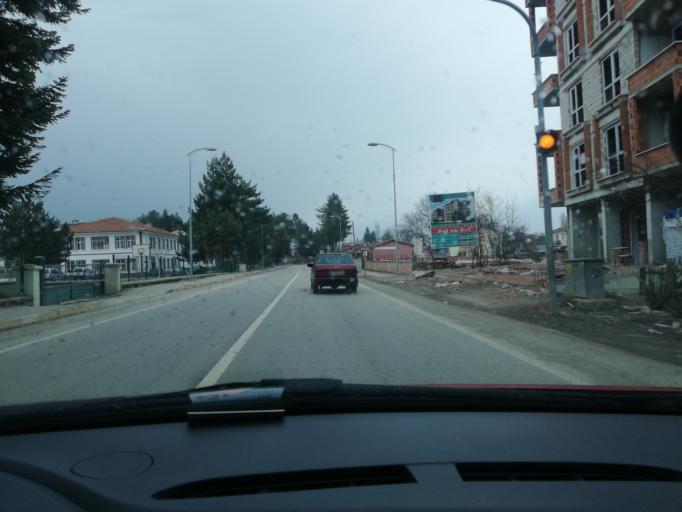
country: TR
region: Kastamonu
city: Daday
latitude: 41.4788
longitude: 33.4732
